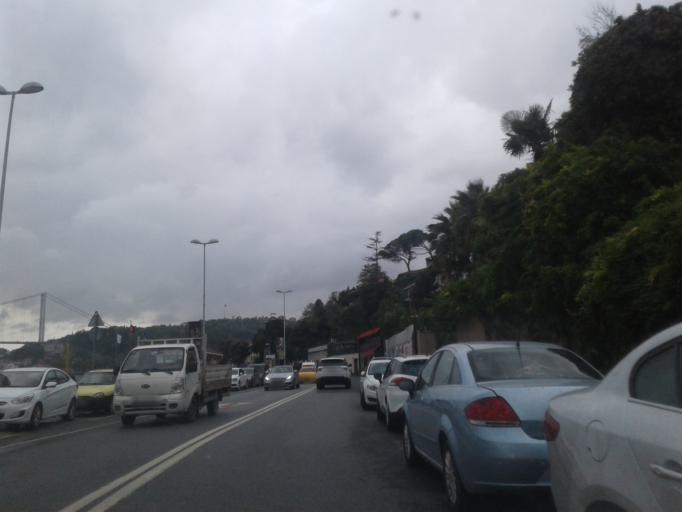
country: TR
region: Istanbul
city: Sisli
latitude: 41.1037
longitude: 29.0564
